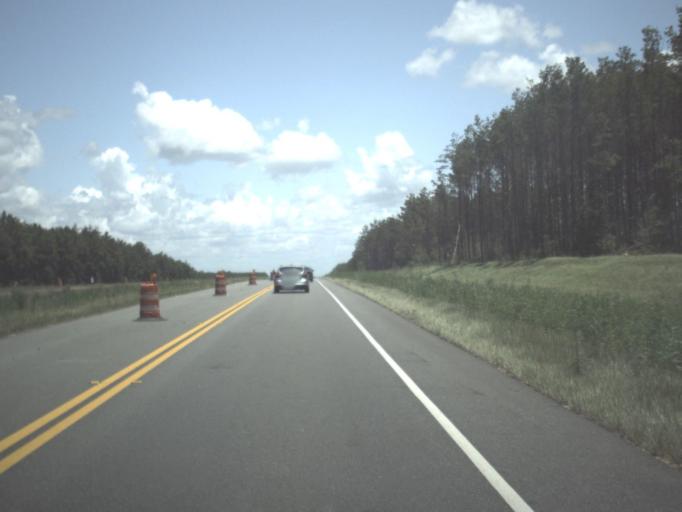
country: US
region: Florida
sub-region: Walton County
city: Freeport
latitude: 30.5056
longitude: -86.1150
